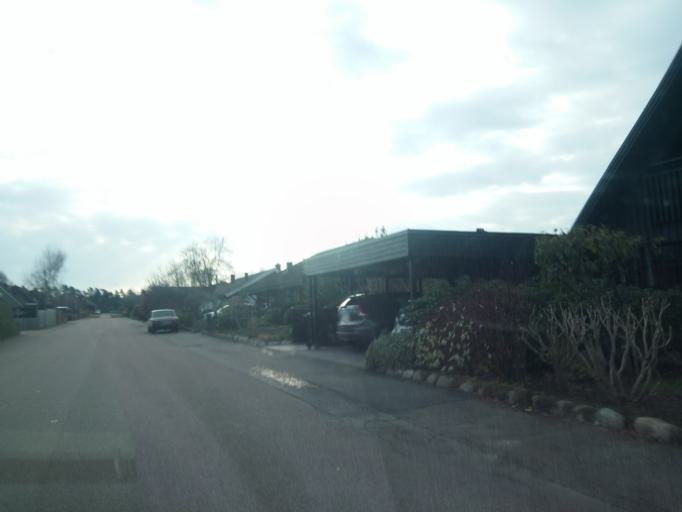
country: SE
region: Skane
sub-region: Angelholms Kommun
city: AEngelholm
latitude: 56.2319
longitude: 12.8375
